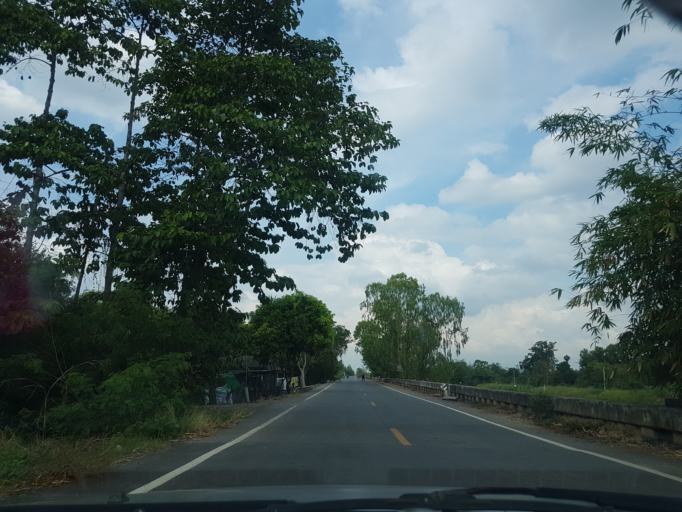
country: TH
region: Pathum Thani
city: Nong Suea
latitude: 14.1921
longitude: 100.8915
